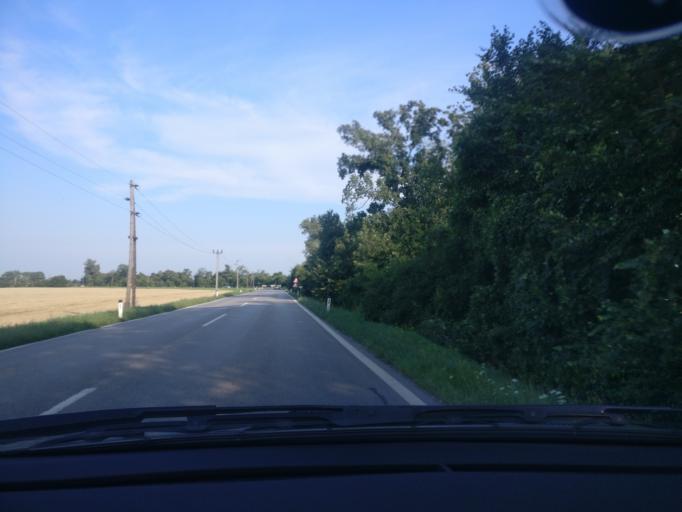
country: AT
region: Lower Austria
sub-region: Politischer Bezirk Modling
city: Laxenburg
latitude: 48.0519
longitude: 16.3536
